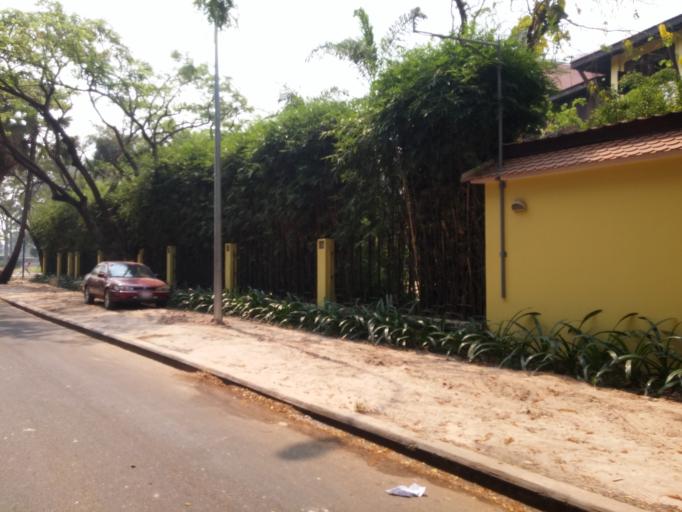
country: KH
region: Siem Reap
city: Siem Reap
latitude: 13.3642
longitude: 103.8579
